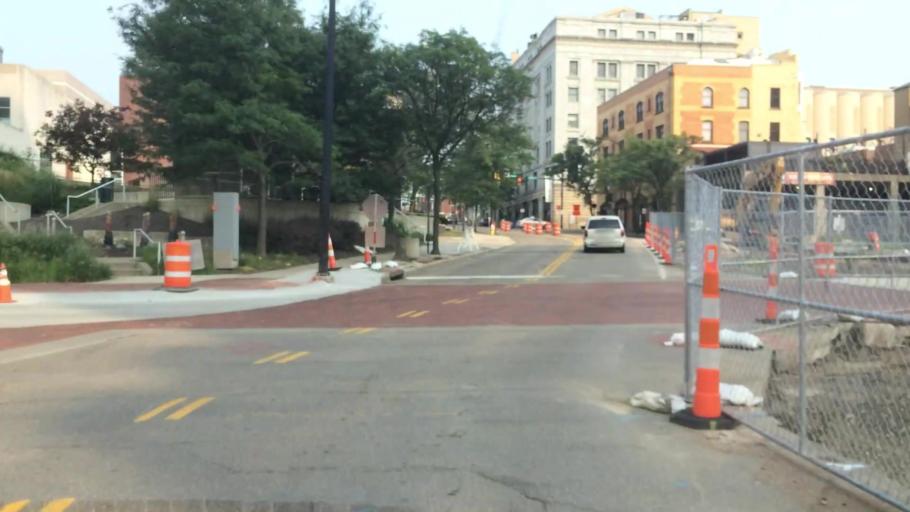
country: US
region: Ohio
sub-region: Summit County
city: Akron
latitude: 41.0833
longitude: -81.5206
